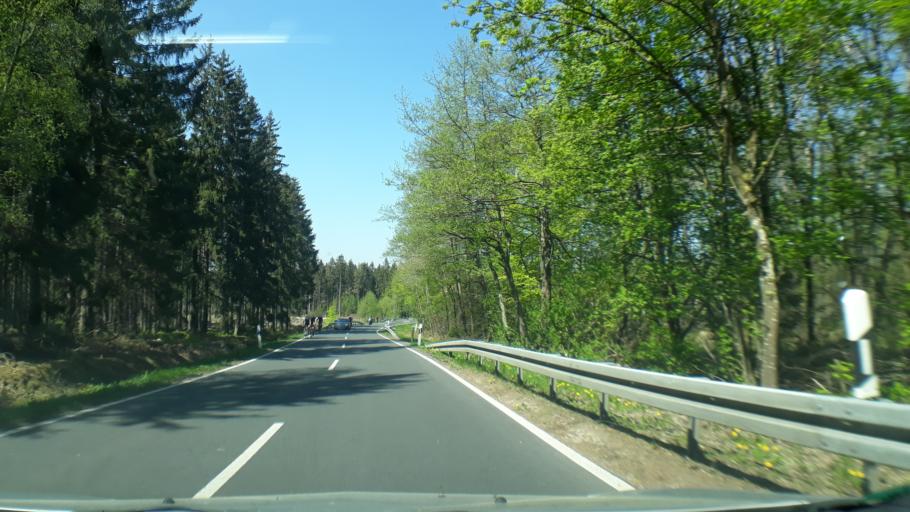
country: DE
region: North Rhine-Westphalia
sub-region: Regierungsbezirk Koln
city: Simmerath
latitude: 50.6463
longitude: 6.2619
